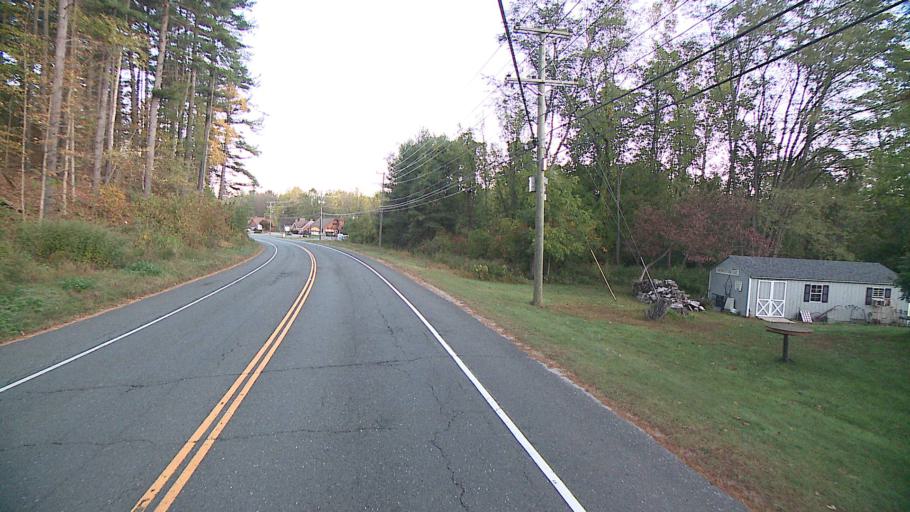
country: US
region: Connecticut
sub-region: Litchfield County
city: New Hartford Center
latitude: 41.8670
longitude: -72.9584
